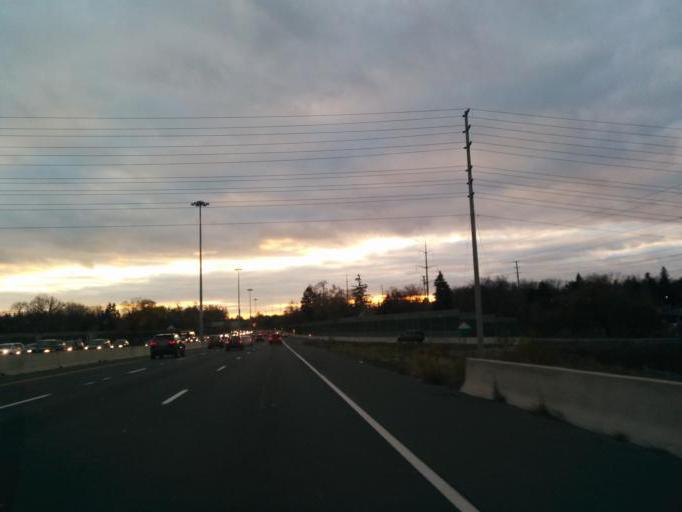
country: CA
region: Ontario
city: Mississauga
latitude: 43.5678
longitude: -79.6006
